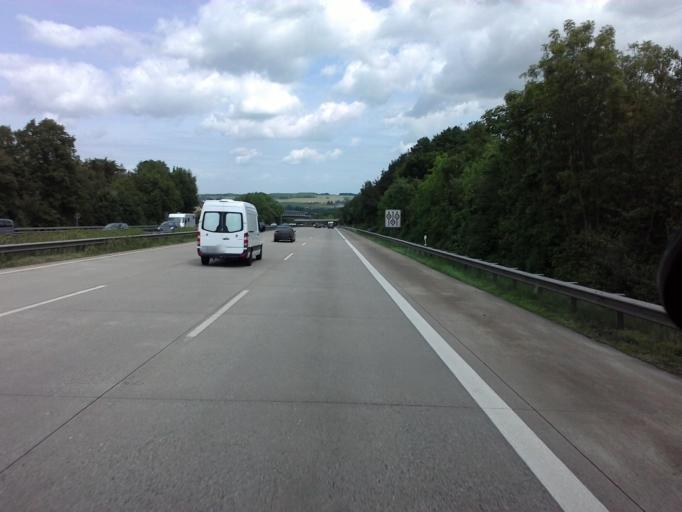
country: DE
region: Rheinland-Pfalz
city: Breitscheid
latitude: 50.6063
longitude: 7.4292
